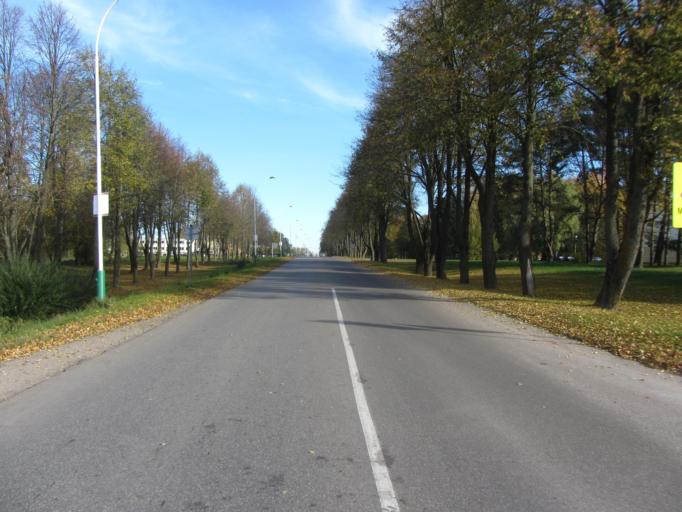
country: LT
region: Vilnius County
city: Elektrenai
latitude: 54.7808
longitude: 24.6529
